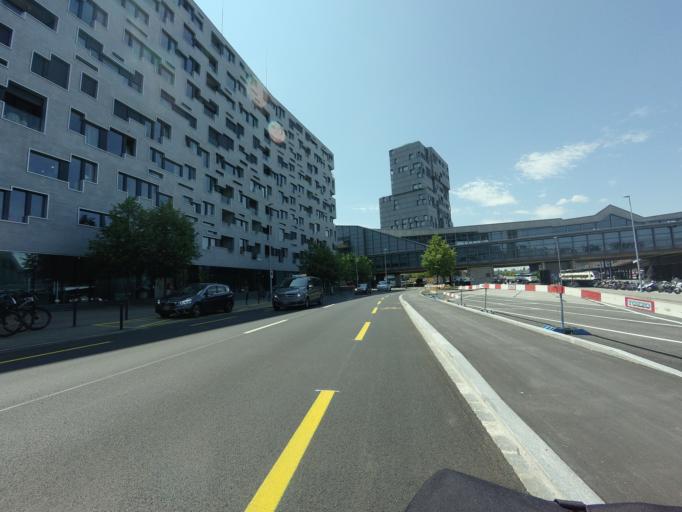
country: CH
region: Basel-City
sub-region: Basel-Stadt
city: Basel
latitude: 47.5458
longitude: 7.5894
